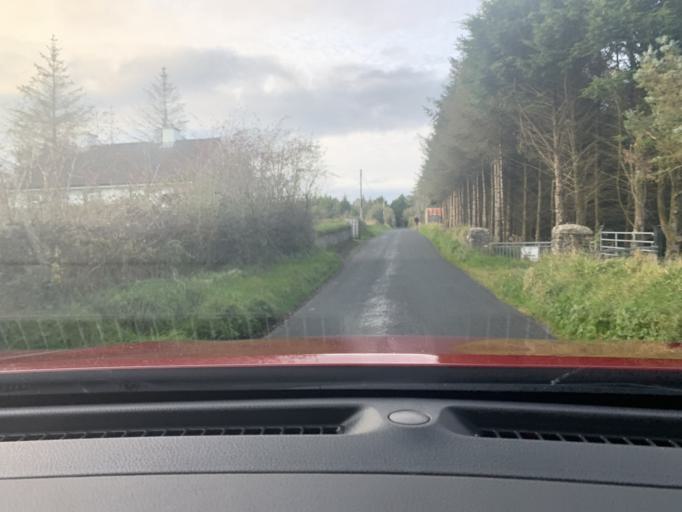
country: IE
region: Connaught
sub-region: Roscommon
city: Ballaghaderreen
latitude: 53.9123
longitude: -8.5857
